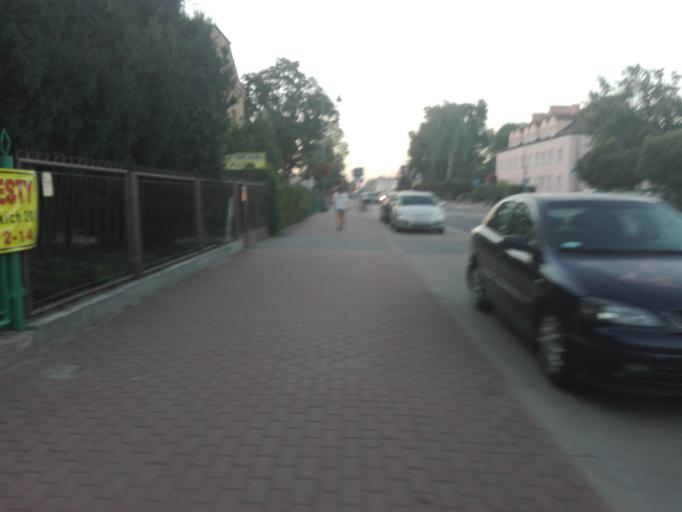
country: PL
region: Masovian Voivodeship
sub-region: Powiat sochaczewski
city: Sochaczew
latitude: 52.2238
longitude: 20.2362
